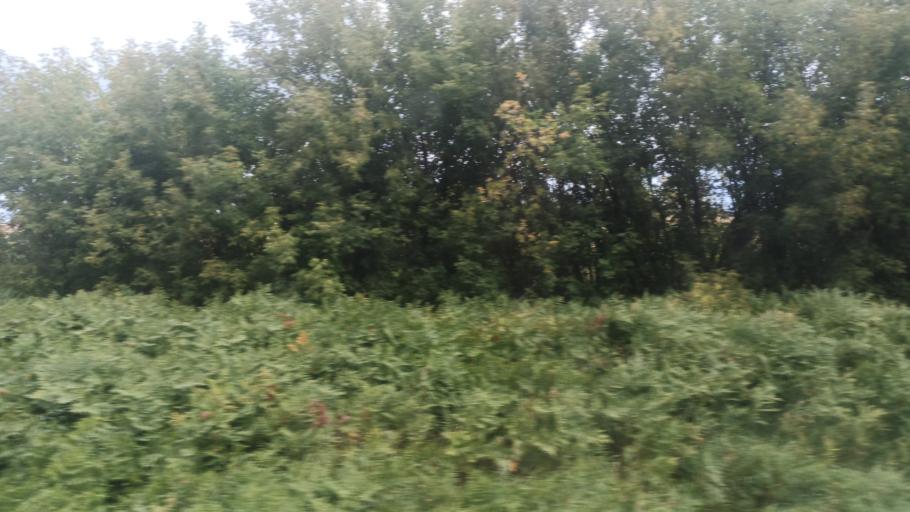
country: RU
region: Altai Krai
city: Nalobikha
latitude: 53.2338
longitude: 84.5121
